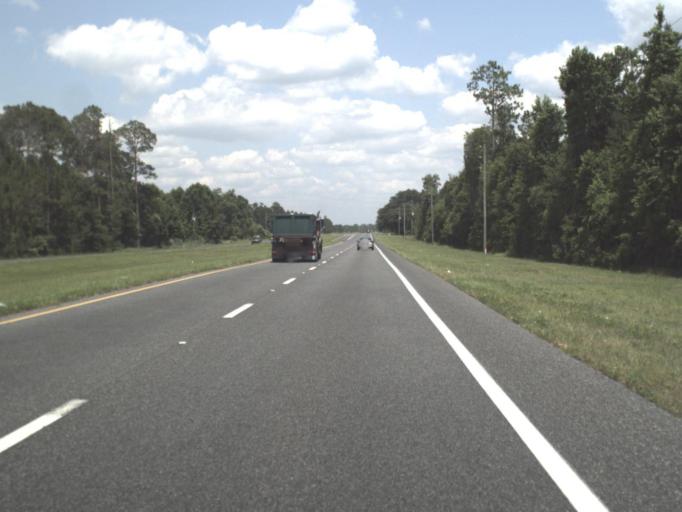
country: US
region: Florida
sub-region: Alachua County
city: Hawthorne
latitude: 29.5987
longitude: -82.1245
